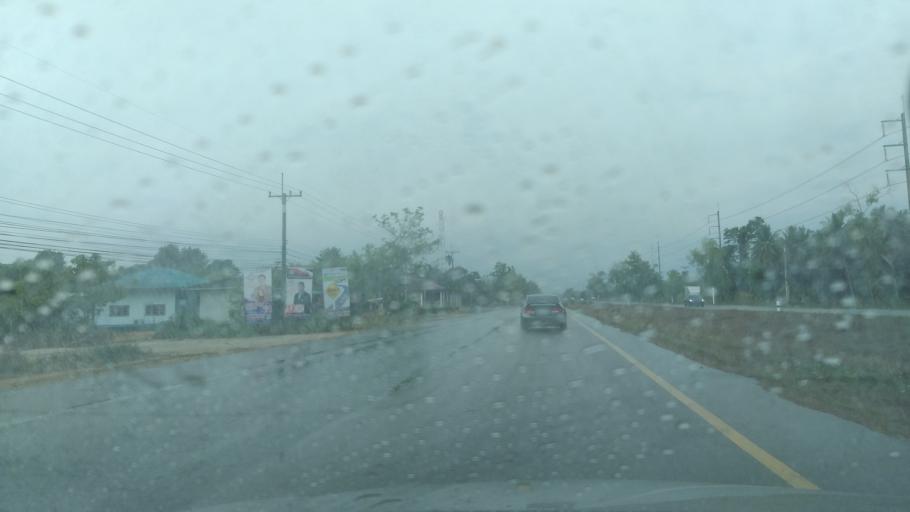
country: TH
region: Trat
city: Khao Saming
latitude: 12.3984
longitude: 102.3492
